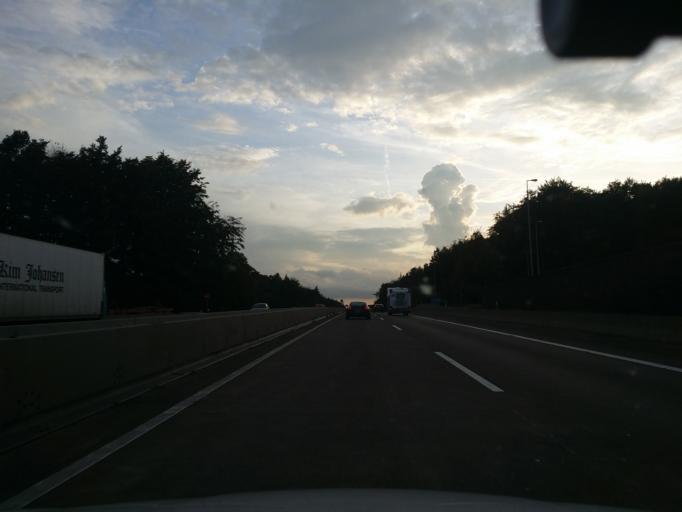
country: DE
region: Hesse
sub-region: Regierungsbezirk Giessen
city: Rabenau
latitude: 50.6228
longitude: 8.8951
